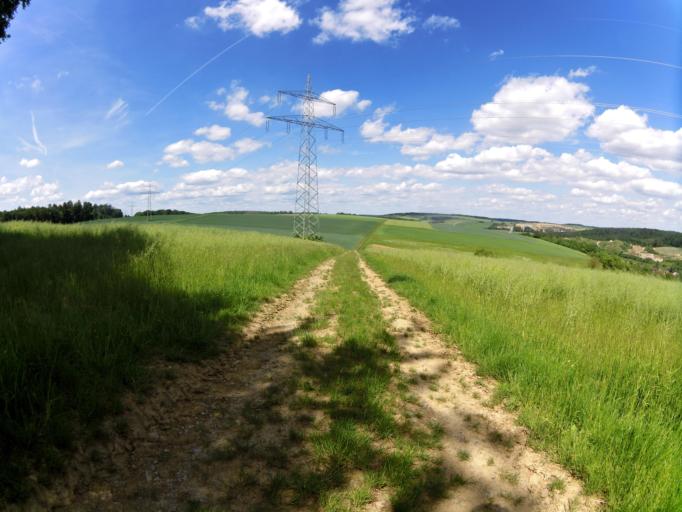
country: DE
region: Bavaria
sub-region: Regierungsbezirk Unterfranken
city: Uettingen
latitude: 49.7800
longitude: 9.7621
